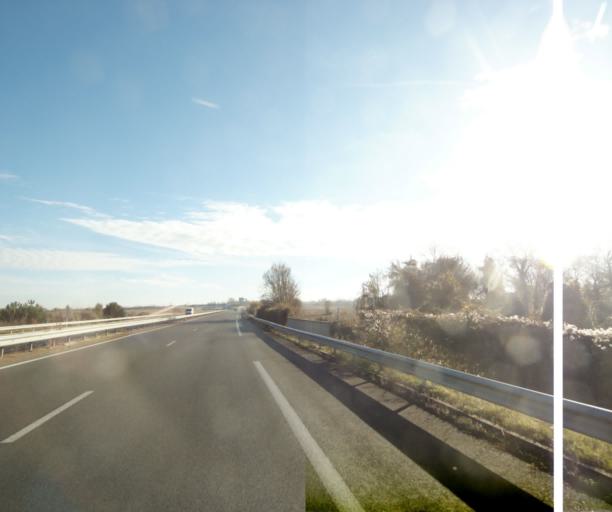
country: FR
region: Poitou-Charentes
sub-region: Departement de la Charente-Maritime
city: Corme-Royal
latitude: 45.7046
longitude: -0.7805
